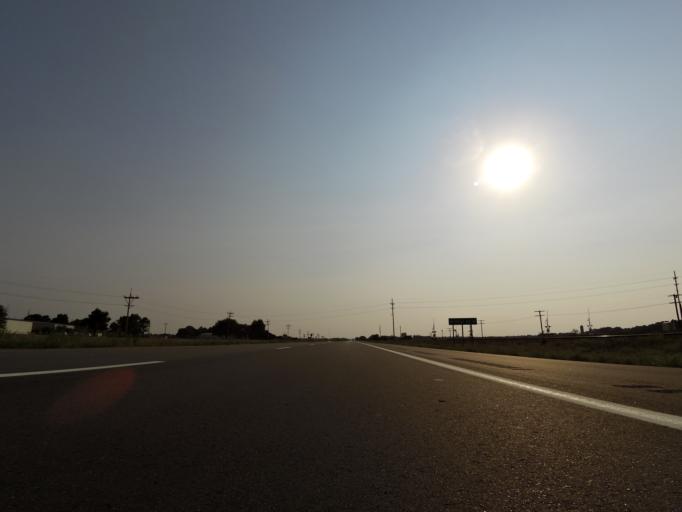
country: US
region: Kansas
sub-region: Reno County
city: South Hutchinson
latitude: 37.9985
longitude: -98.0305
